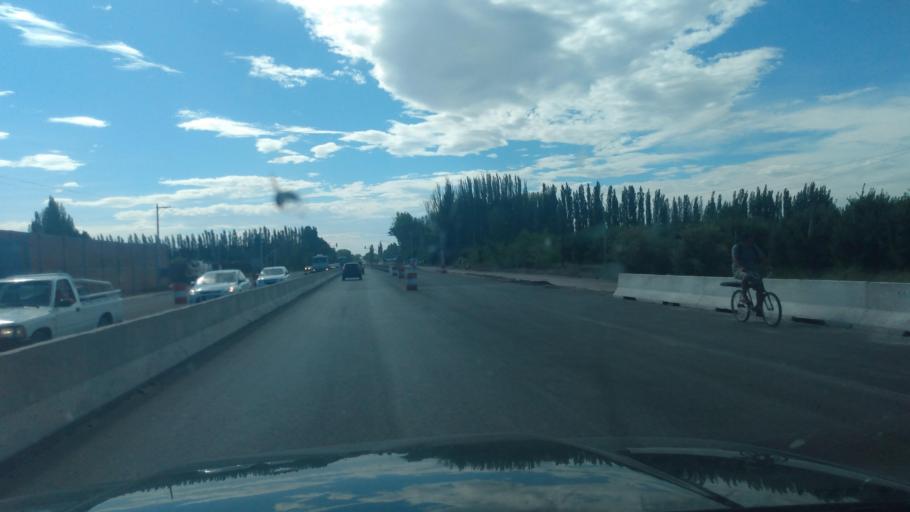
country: AR
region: Rio Negro
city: Cipolletti
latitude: -38.9608
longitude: -67.9752
